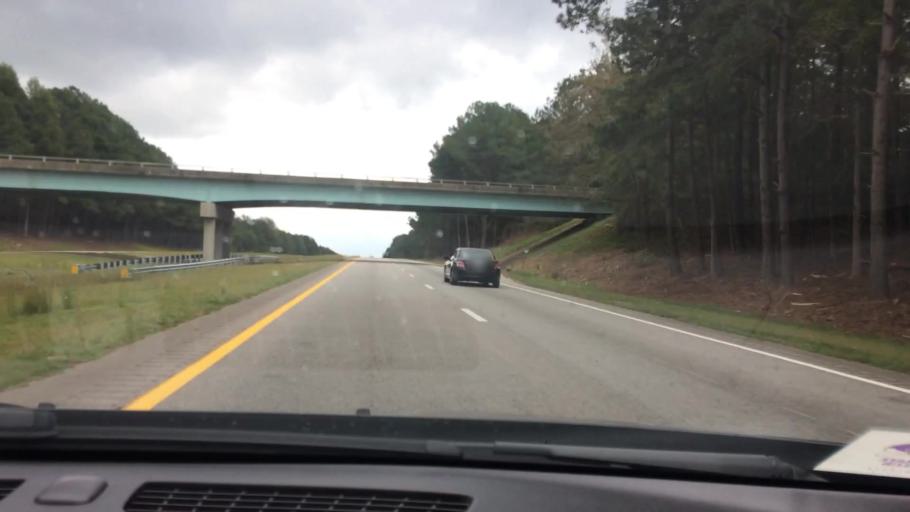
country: US
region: North Carolina
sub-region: Wake County
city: Zebulon
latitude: 35.8101
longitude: -78.2243
